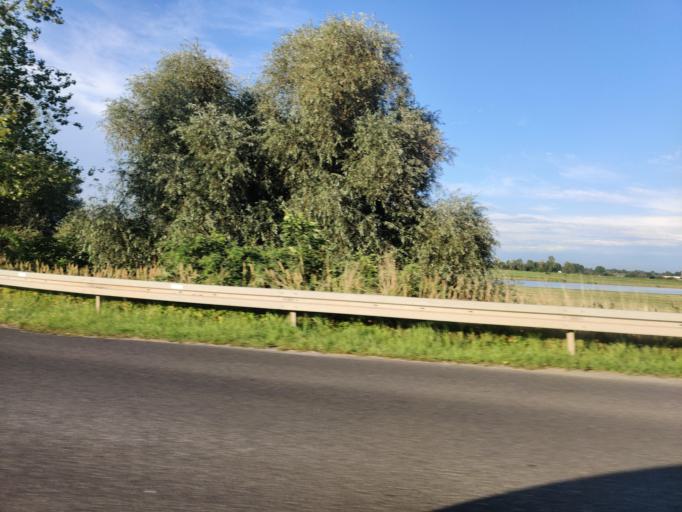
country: PL
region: Greater Poland Voivodeship
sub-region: Konin
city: Konin
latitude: 52.2115
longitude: 18.2609
